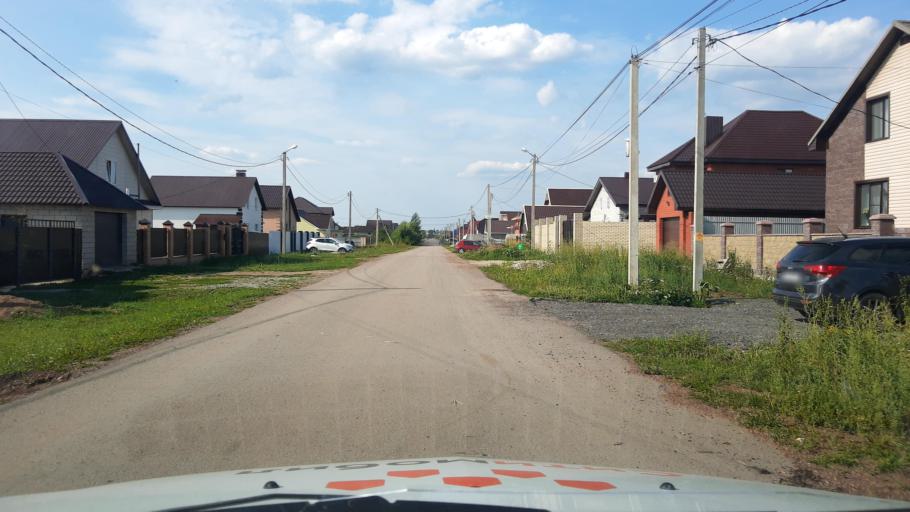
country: RU
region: Bashkortostan
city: Kabakovo
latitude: 54.6587
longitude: 56.2122
